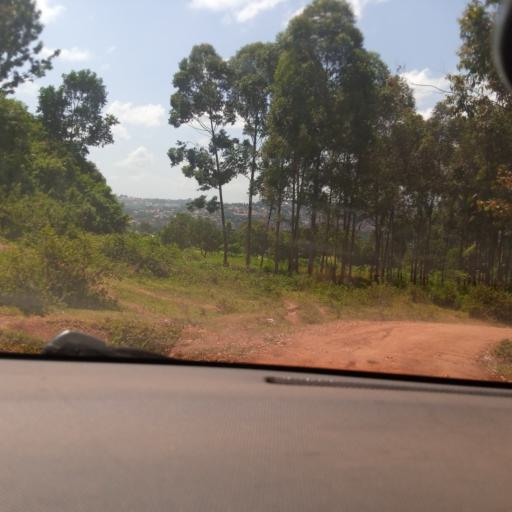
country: UG
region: Central Region
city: Masaka
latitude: -0.3228
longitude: 31.7435
